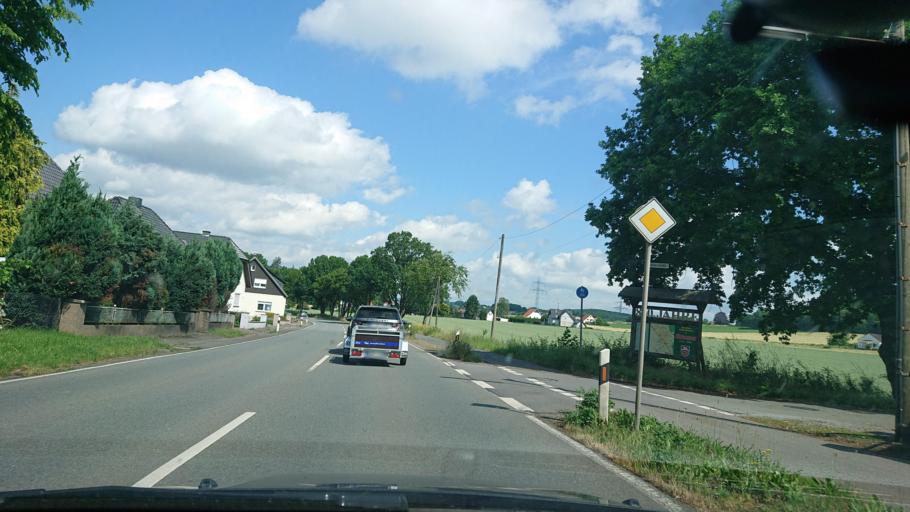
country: DE
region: North Rhine-Westphalia
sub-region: Regierungsbezirk Detmold
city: Hiddenhausen
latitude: 52.1570
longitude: 8.6426
